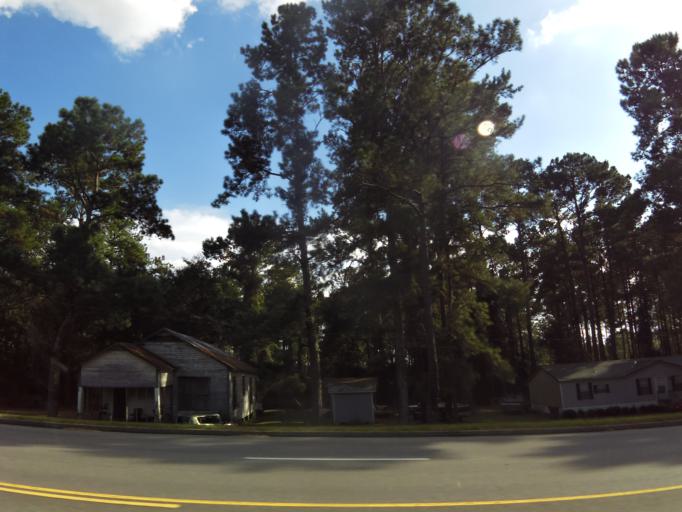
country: US
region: Georgia
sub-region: Brooks County
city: Quitman
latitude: 30.7859
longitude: -83.5874
